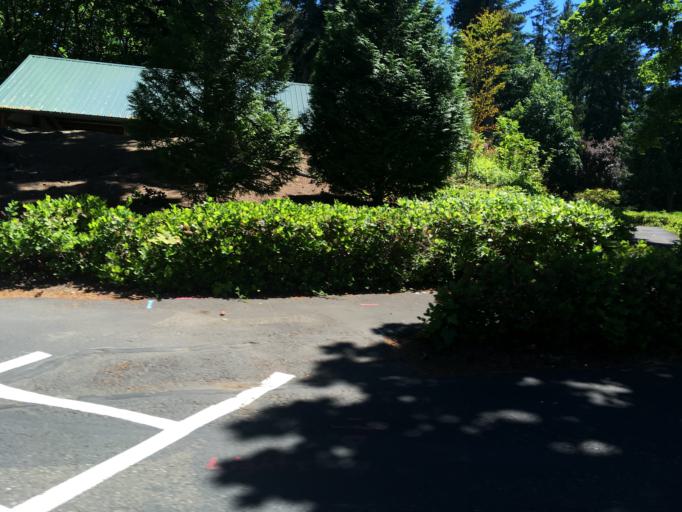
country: US
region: Washington
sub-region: King County
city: Redmond
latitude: 47.6299
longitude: -122.1281
